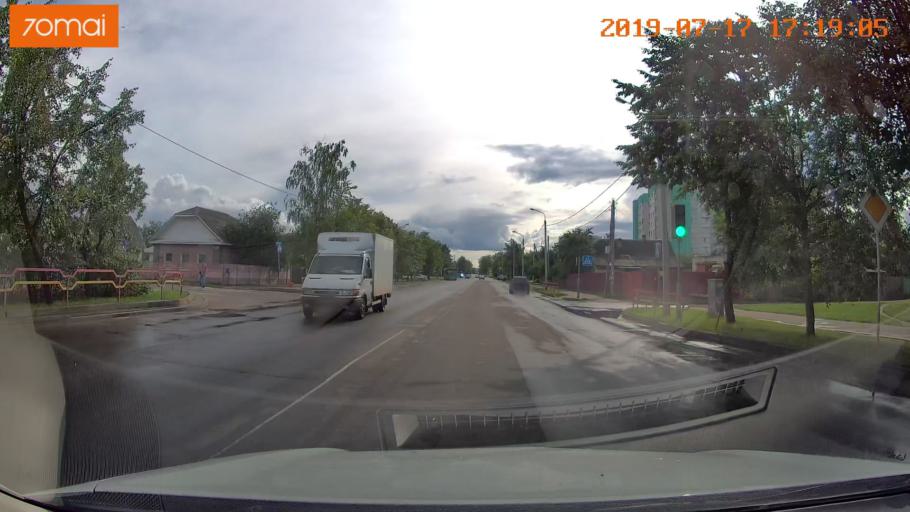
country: BY
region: Mogilev
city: Babruysk
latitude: 53.1585
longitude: 29.1950
